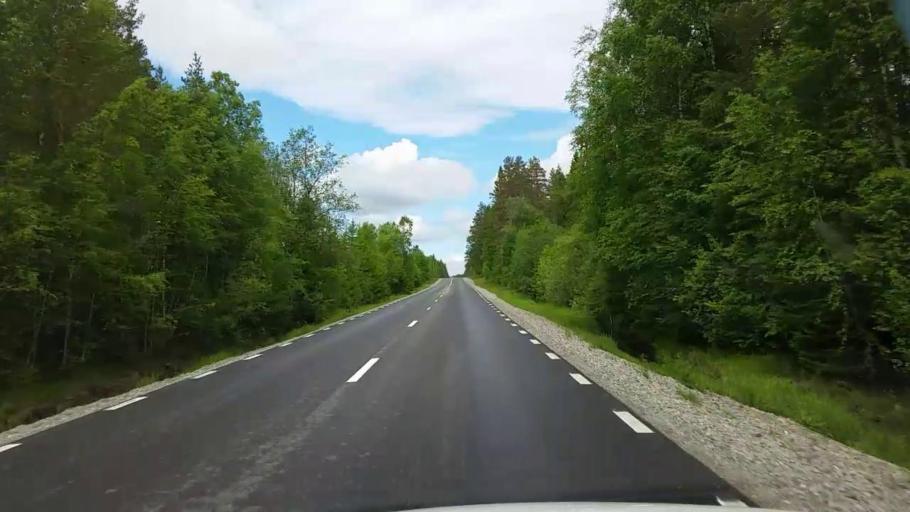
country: SE
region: Gaevleborg
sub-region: Sandvikens Kommun
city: Jarbo
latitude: 60.9089
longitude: 16.3758
